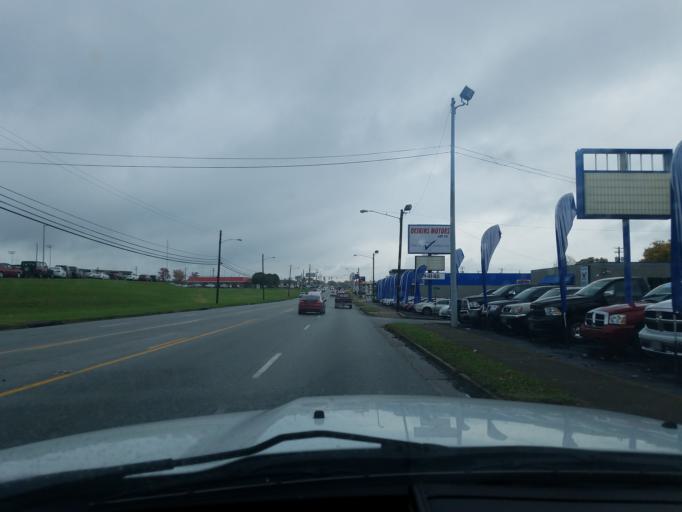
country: US
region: Kentucky
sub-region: Taylor County
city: Campbellsville
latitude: 37.3493
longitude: -85.3342
